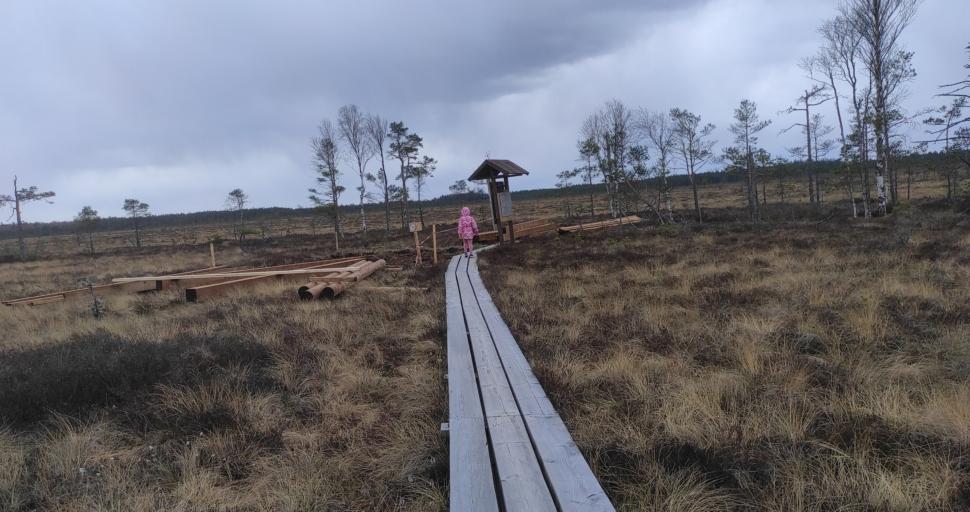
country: LV
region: Dundaga
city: Dundaga
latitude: 57.3445
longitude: 22.1565
